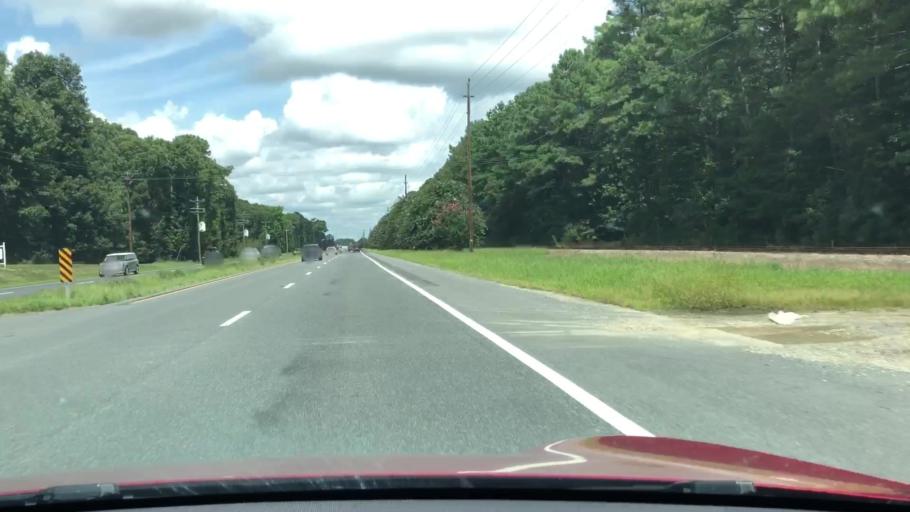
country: US
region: Virginia
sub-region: Northampton County
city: Exmore
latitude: 37.5021
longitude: -75.8405
